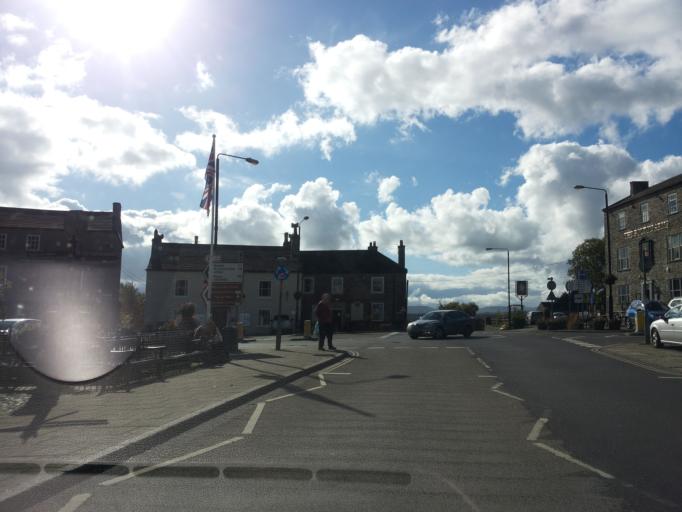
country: GB
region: England
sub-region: North Yorkshire
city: Leyburn
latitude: 54.3101
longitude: -1.8304
